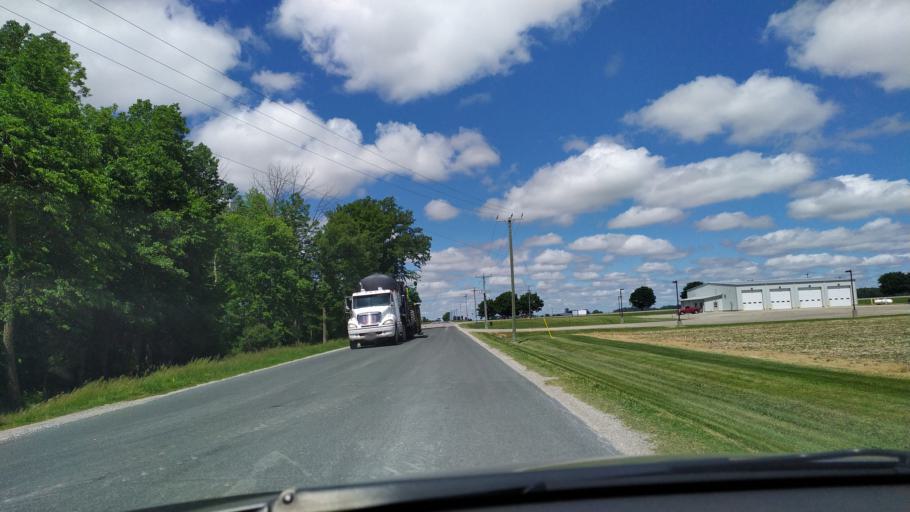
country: CA
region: Ontario
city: Huron East
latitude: 43.4571
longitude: -81.1775
